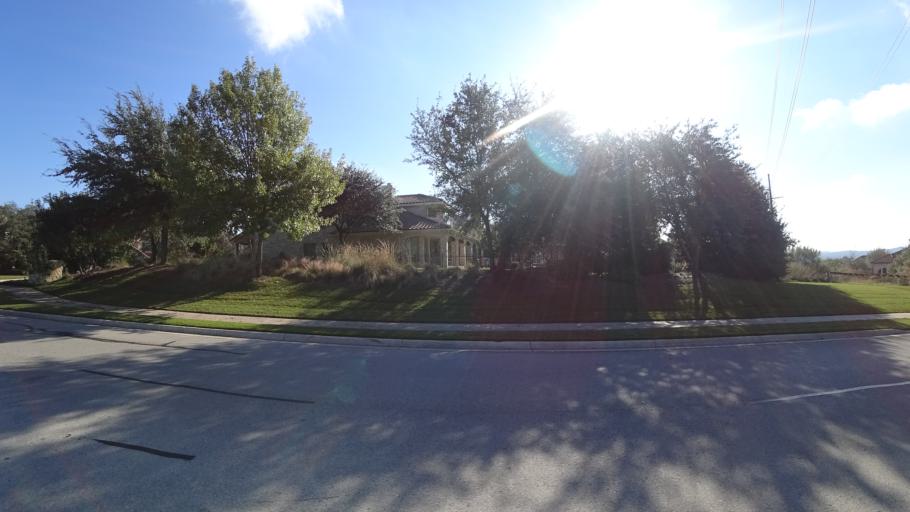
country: US
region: Texas
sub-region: Travis County
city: Hudson Bend
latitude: 30.3600
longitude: -97.8879
